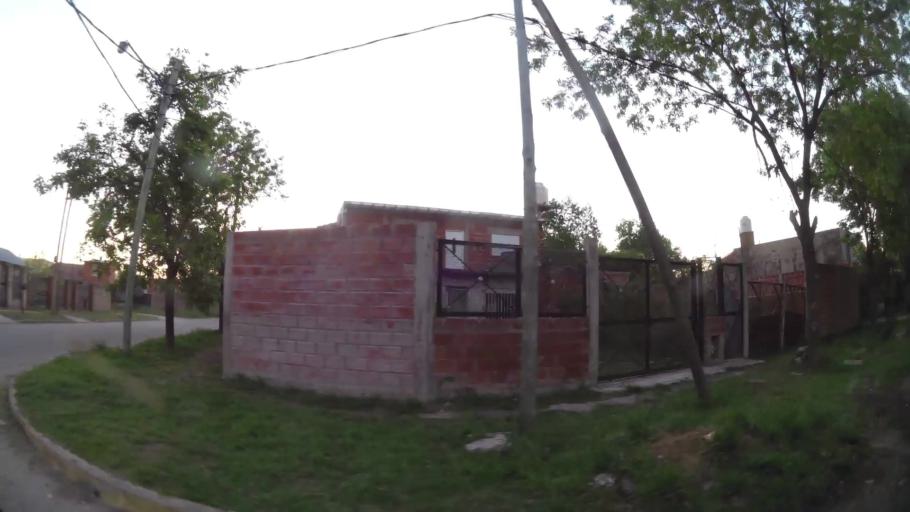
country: AR
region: Buenos Aires
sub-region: Partido de Almirante Brown
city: Adrogue
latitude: -34.7950
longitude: -58.3204
